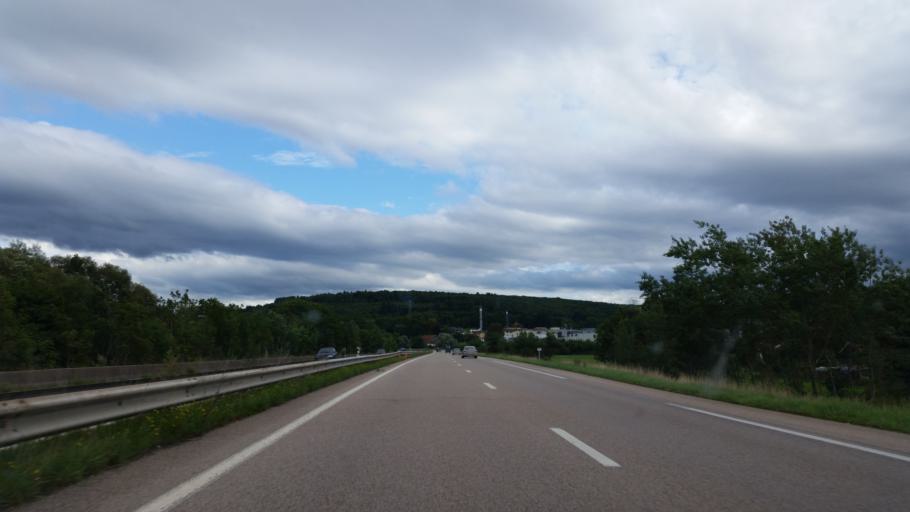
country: FR
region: Lorraine
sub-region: Departement des Vosges
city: Archettes
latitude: 48.1202
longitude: 6.5337
